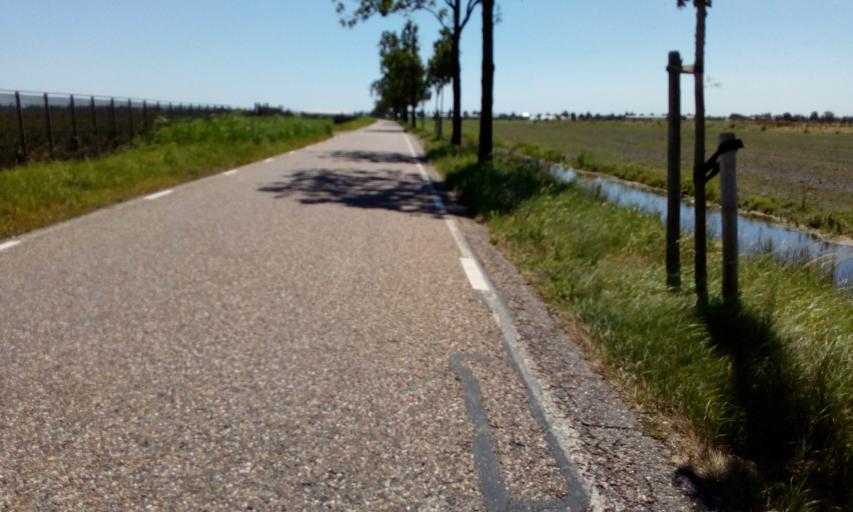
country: NL
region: South Holland
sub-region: Gemeente Alphen aan den Rijn
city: Alphen aan den Rijn
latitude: 52.1028
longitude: 4.6869
